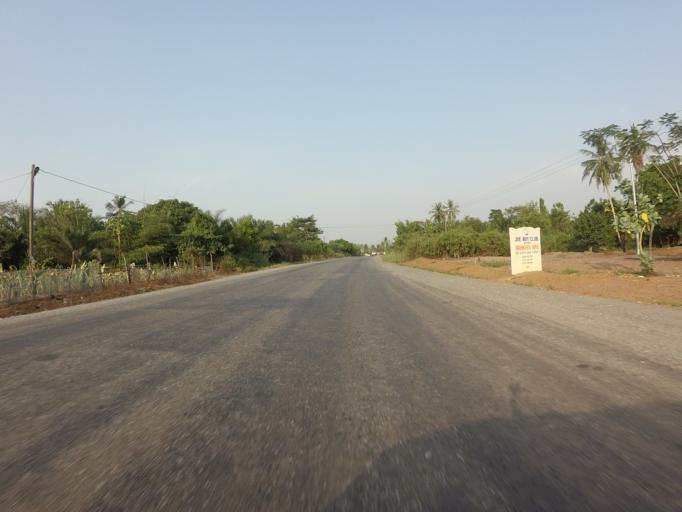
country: GH
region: Volta
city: Ho
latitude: 6.4448
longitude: 0.2087
